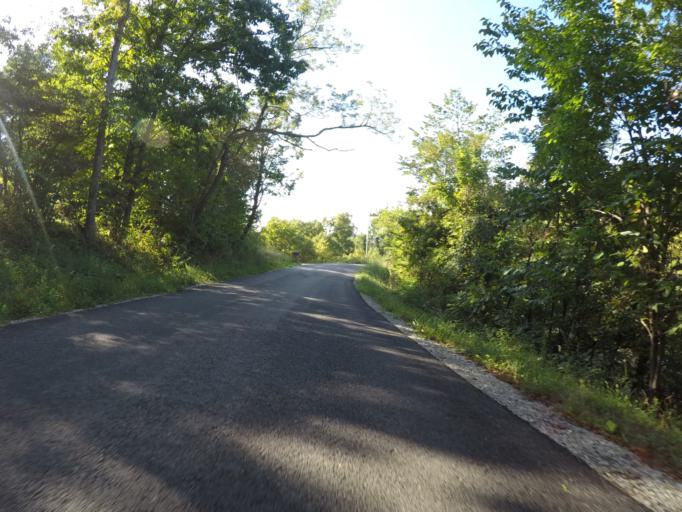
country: US
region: Ohio
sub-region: Lawrence County
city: Burlington
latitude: 38.5238
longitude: -82.5243
